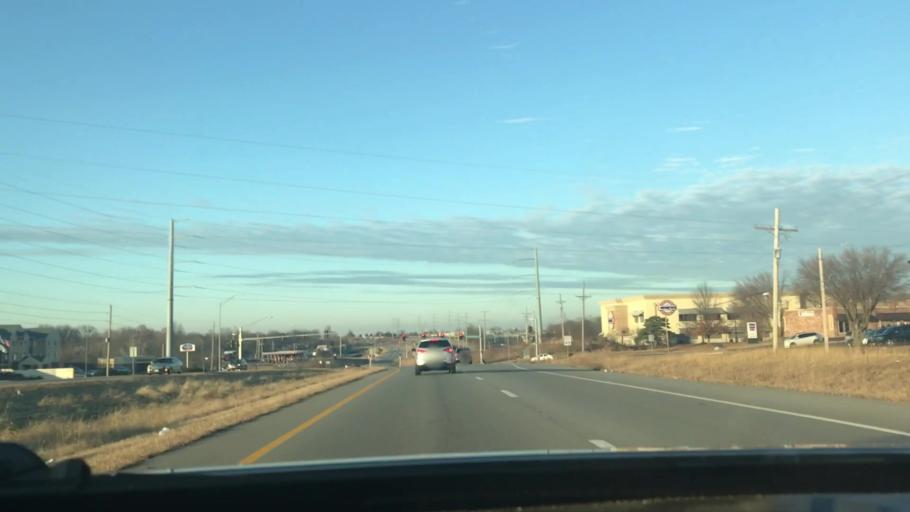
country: US
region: Missouri
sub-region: Jackson County
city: Lees Summit
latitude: 38.9339
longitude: -94.3598
